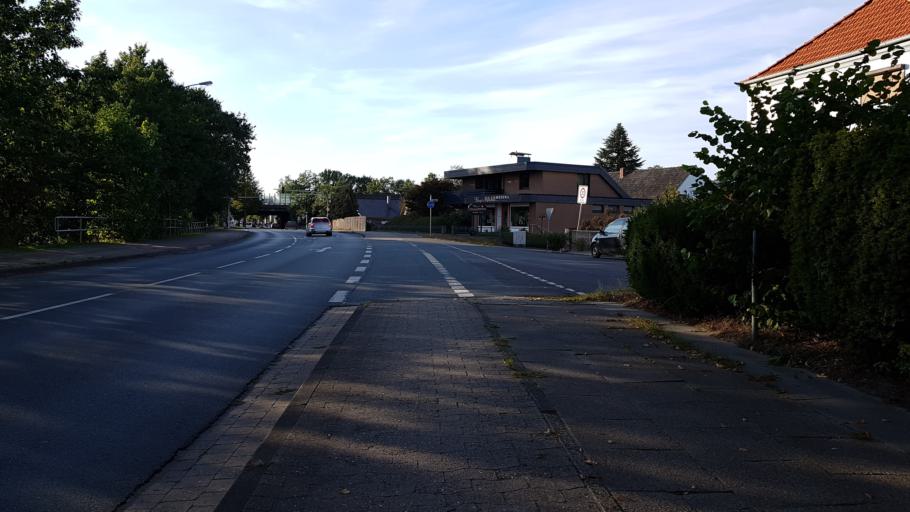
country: DE
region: Lower Saxony
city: Oyten
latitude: 53.0303
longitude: 8.9651
